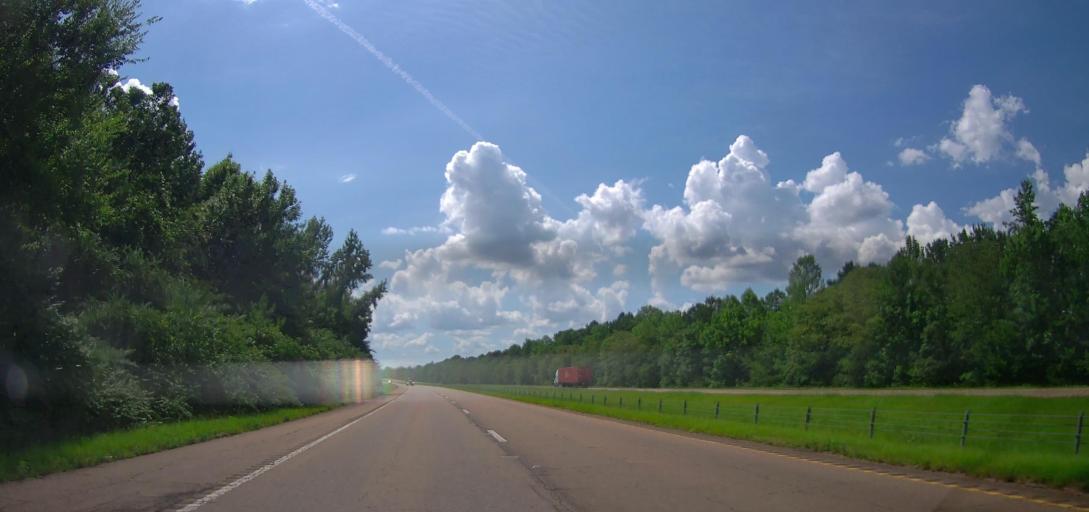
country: US
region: Mississippi
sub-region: Lowndes County
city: New Hope
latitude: 33.5088
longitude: -88.3269
